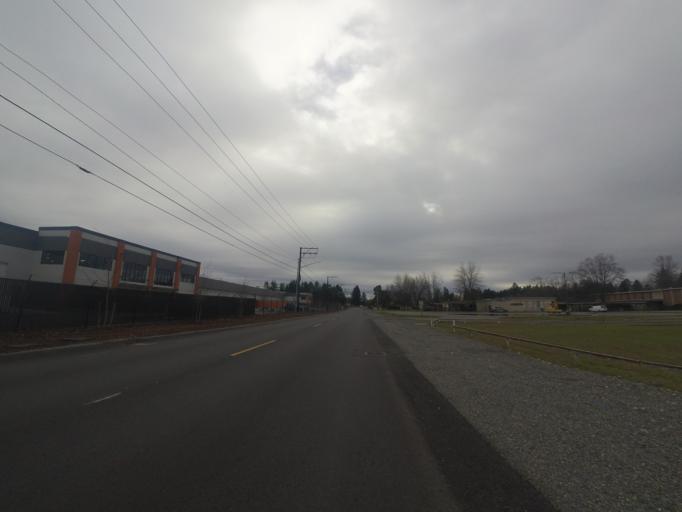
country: US
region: Washington
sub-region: Pierce County
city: Fort Lewis
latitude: 47.1235
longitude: -122.5375
